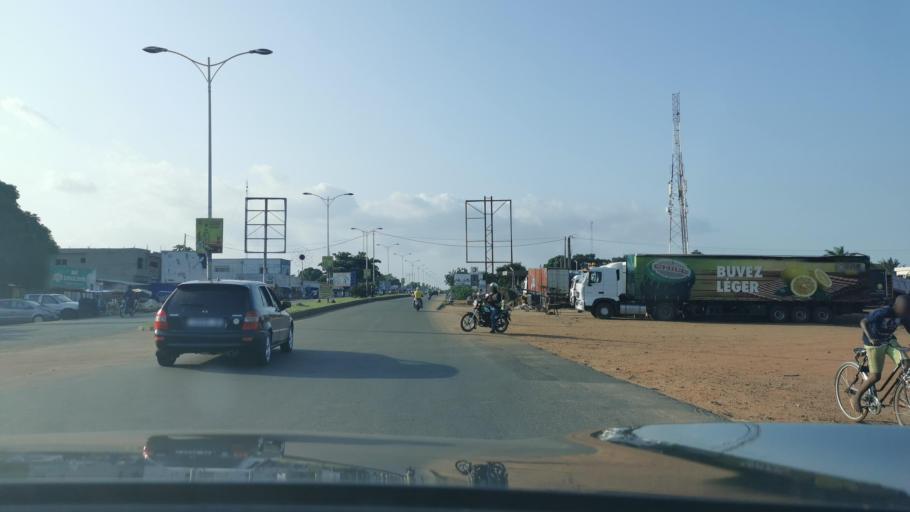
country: TG
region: Maritime
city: Lome
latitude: 6.2144
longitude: 1.2087
